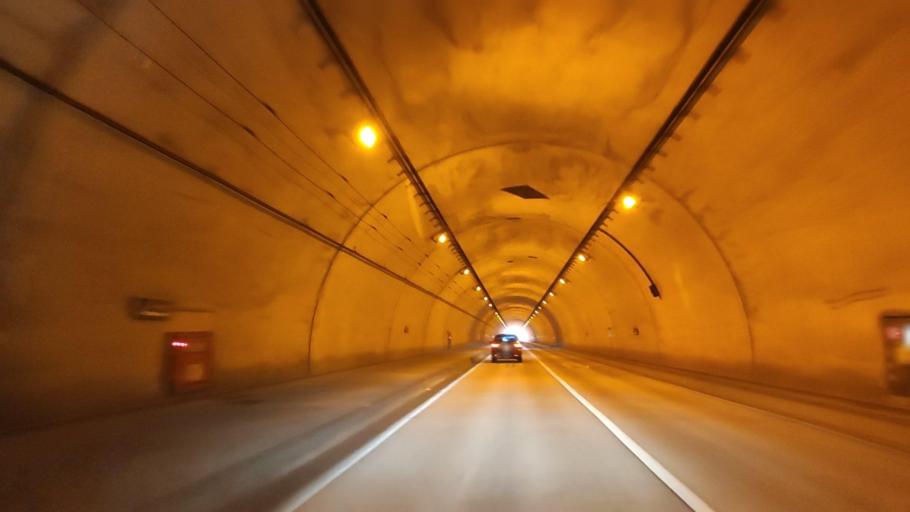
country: JP
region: Ehime
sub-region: Shikoku-chuo Shi
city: Matsuyama
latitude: 33.8844
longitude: 132.7088
